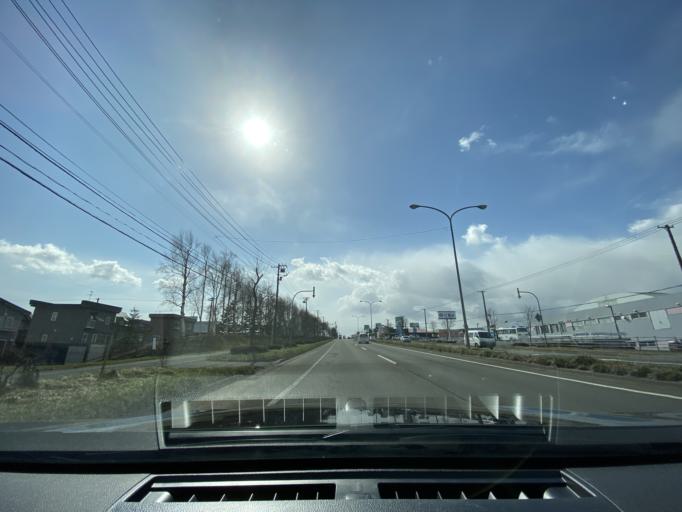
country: JP
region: Hokkaido
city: Kitahiroshima
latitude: 42.9653
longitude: 141.4863
